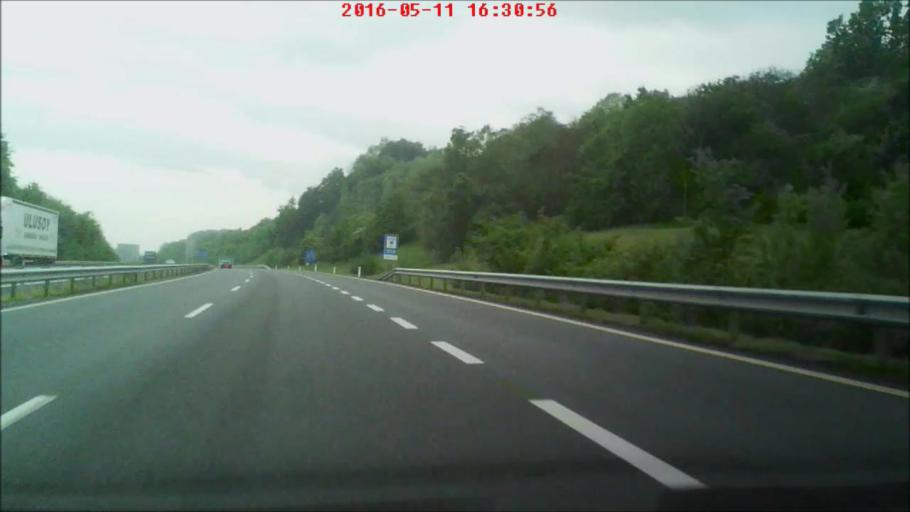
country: SI
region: Sentilj
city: Sentilj v Slov. Goricah
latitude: 46.6745
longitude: 15.6466
